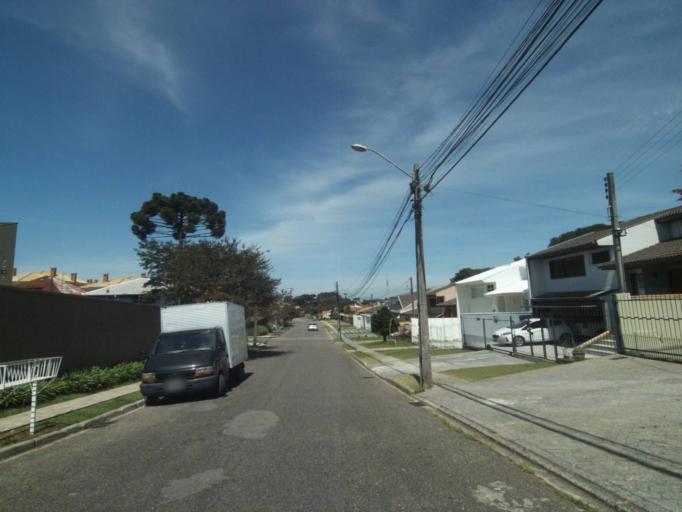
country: BR
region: Parana
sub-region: Curitiba
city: Curitiba
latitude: -25.4619
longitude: -49.2402
